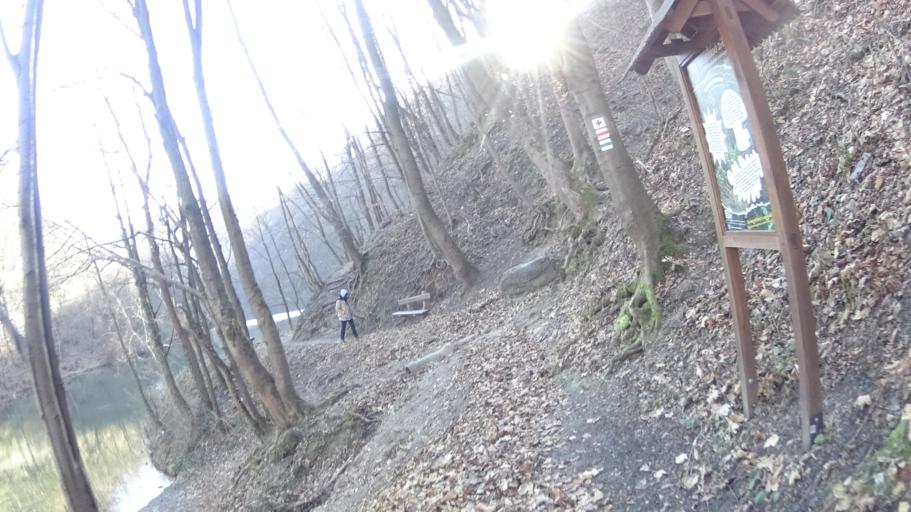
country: HU
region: Borsod-Abauj-Zemplen
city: Sajobabony
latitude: 48.1091
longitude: 20.6145
